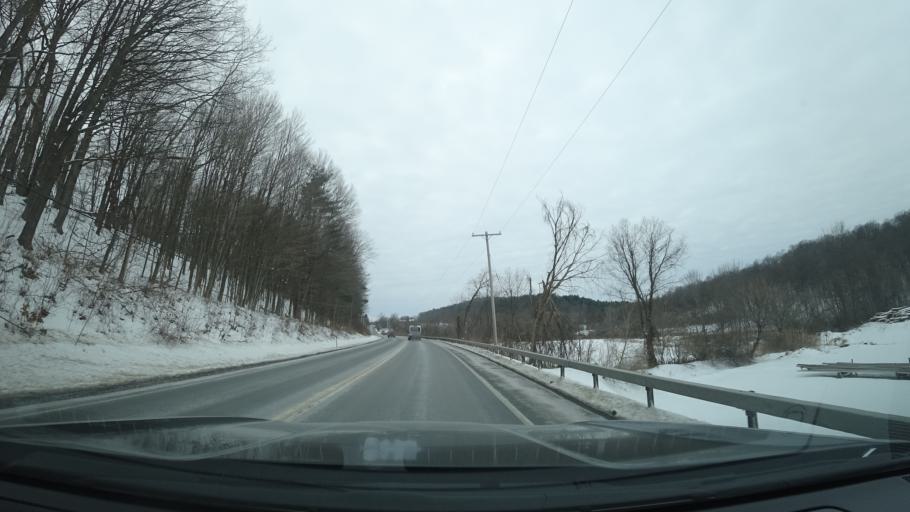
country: US
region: New York
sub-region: Washington County
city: Greenwich
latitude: 43.1886
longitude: -73.4913
